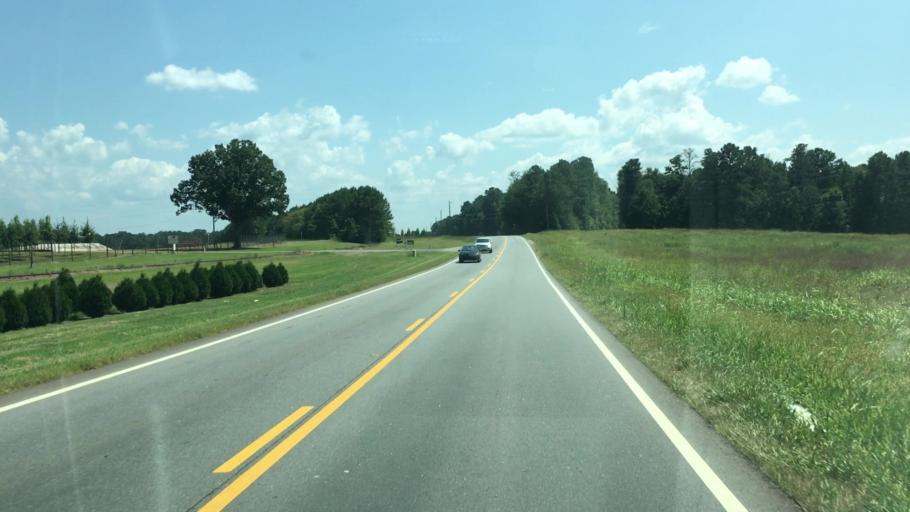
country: US
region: Georgia
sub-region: Oconee County
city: Watkinsville
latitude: 33.7525
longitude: -83.4351
